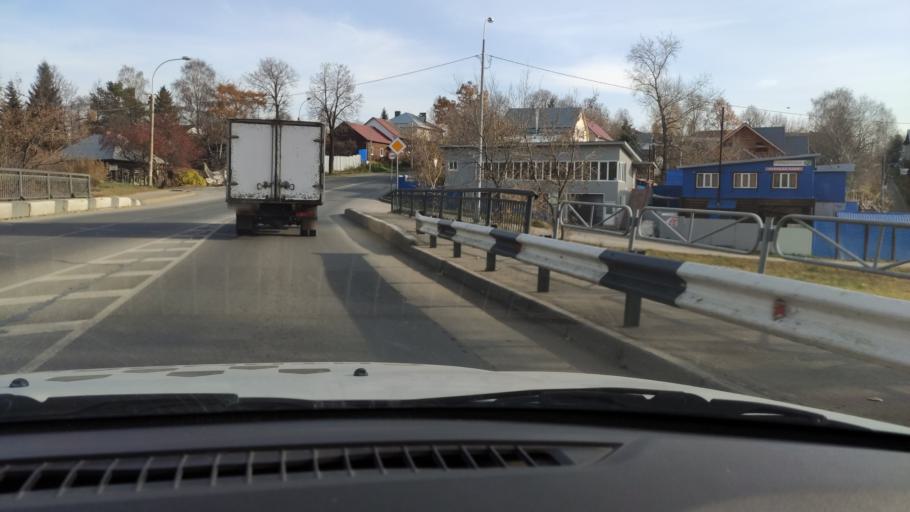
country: RU
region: Perm
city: Perm
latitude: 58.0397
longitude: 56.3279
